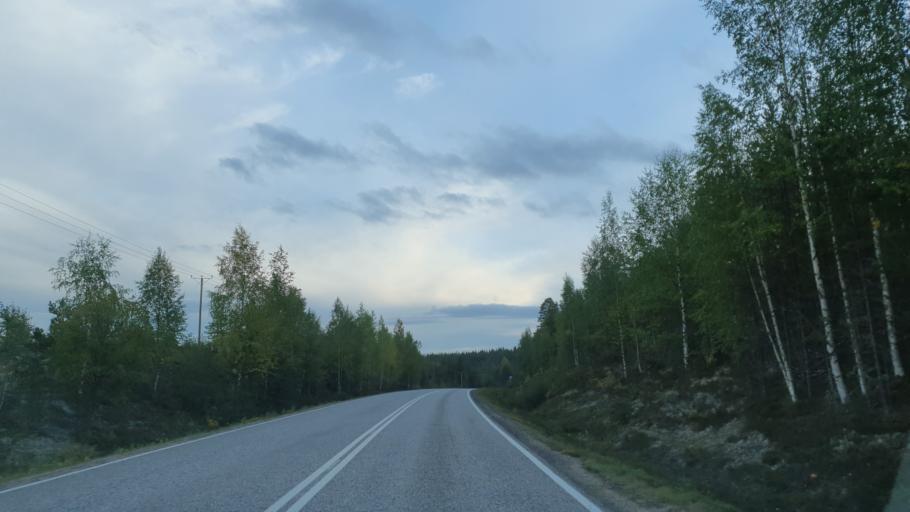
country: FI
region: Kainuu
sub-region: Kehys-Kainuu
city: Kuhmo
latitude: 64.2321
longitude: 29.8191
